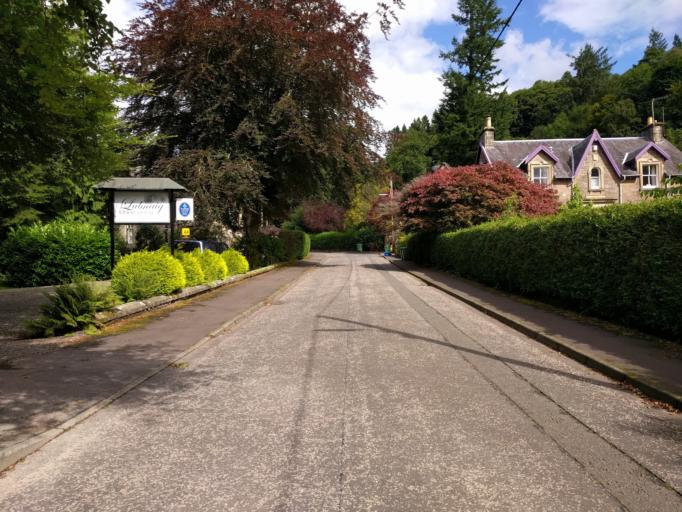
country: GB
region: Scotland
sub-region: Stirling
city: Callander
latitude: 56.2453
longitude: -4.2257
